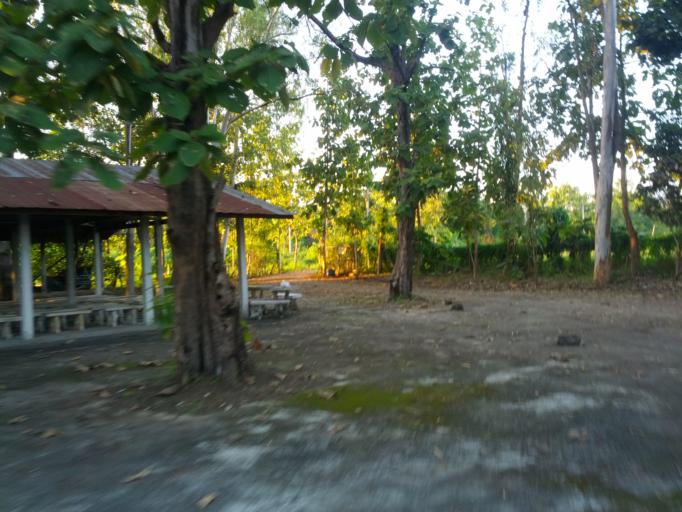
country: TH
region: Chiang Mai
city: San Kamphaeng
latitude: 18.7666
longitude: 99.1168
